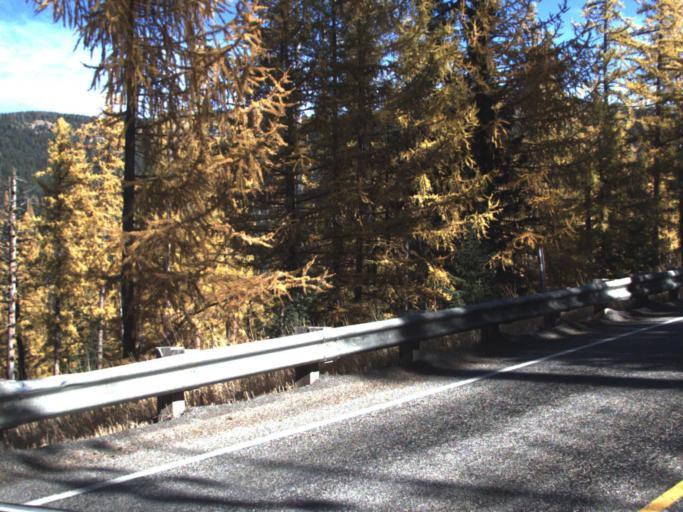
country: US
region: Washington
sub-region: Ferry County
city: Republic
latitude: 48.6038
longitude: -118.5099
